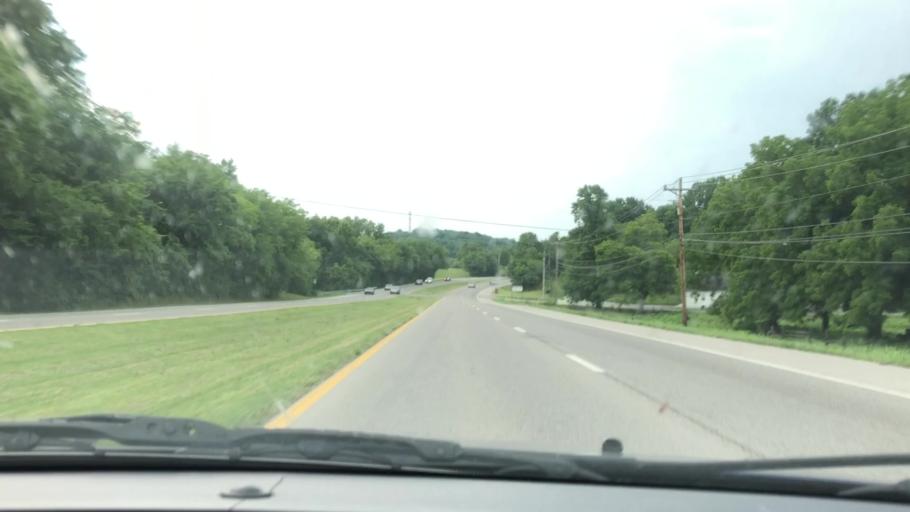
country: US
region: Tennessee
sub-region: Maury County
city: Columbia
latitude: 35.6777
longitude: -86.9993
